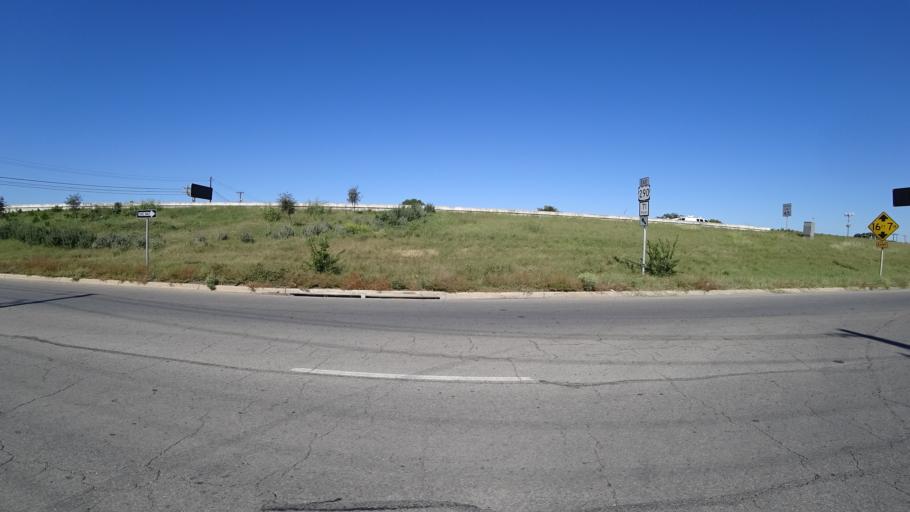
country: US
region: Texas
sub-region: Travis County
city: Rollingwood
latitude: 30.2281
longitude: -97.7855
